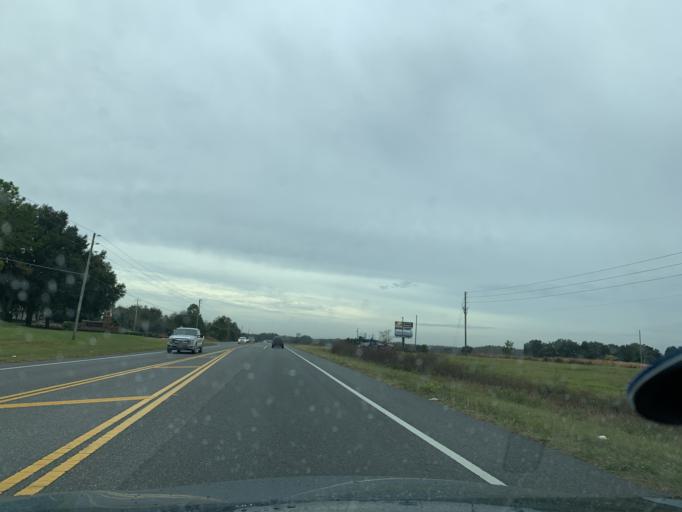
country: US
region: Florida
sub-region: Pasco County
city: Zephyrhills West
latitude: 28.2385
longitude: -82.2462
